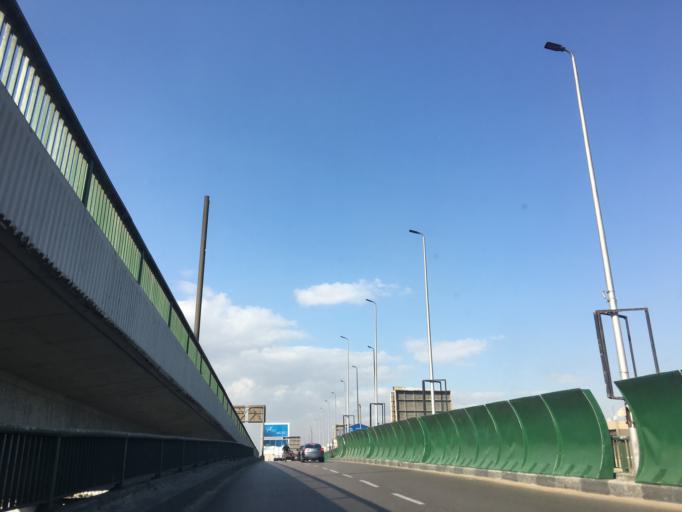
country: EG
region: Muhafazat al Qahirah
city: Cairo
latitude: 30.0598
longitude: 31.3021
